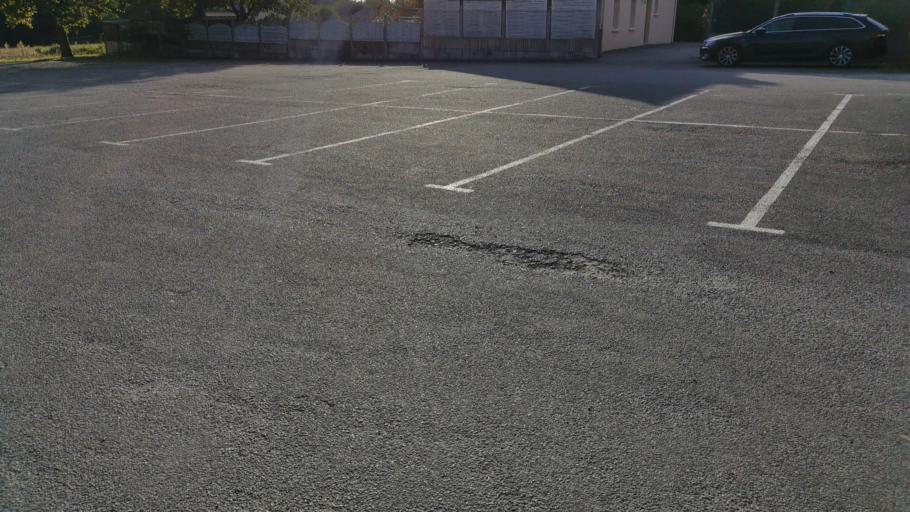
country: FR
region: Pays de la Loire
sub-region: Departement de la Loire-Atlantique
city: Pontchateau
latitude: 47.4213
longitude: -2.1219
